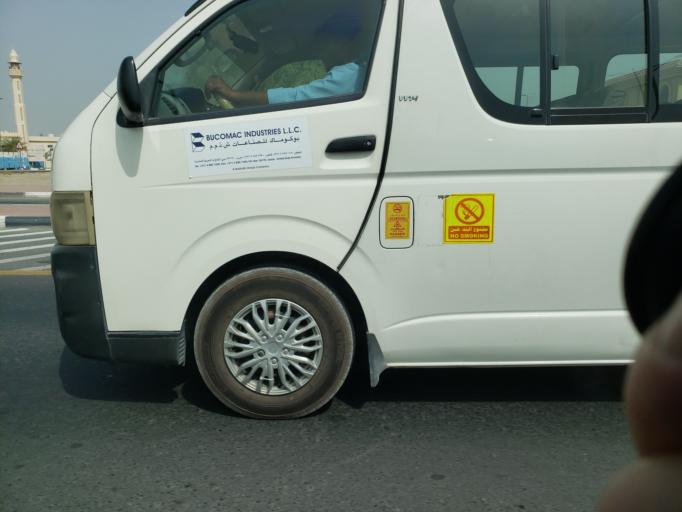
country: AE
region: Ash Shariqah
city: Sharjah
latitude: 25.3645
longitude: 55.4469
